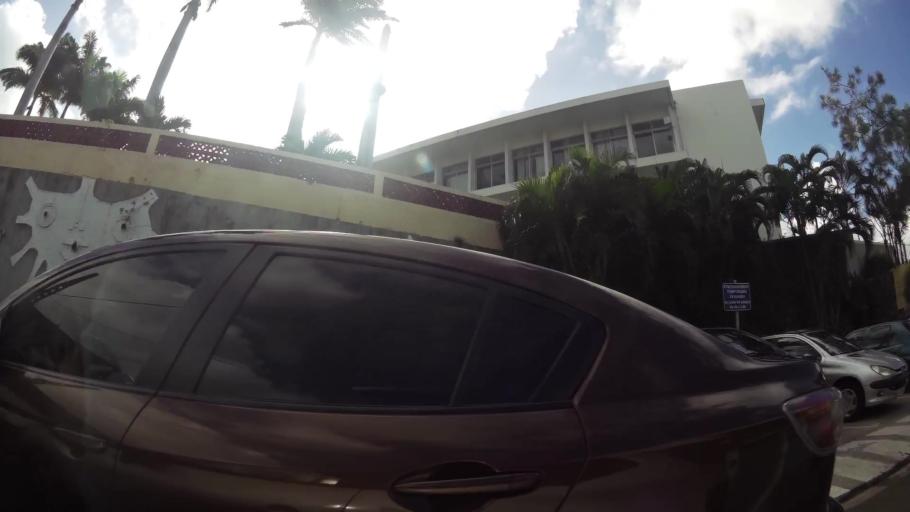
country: MQ
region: Martinique
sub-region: Martinique
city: Le Vauclin
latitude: 14.5453
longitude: -60.8401
